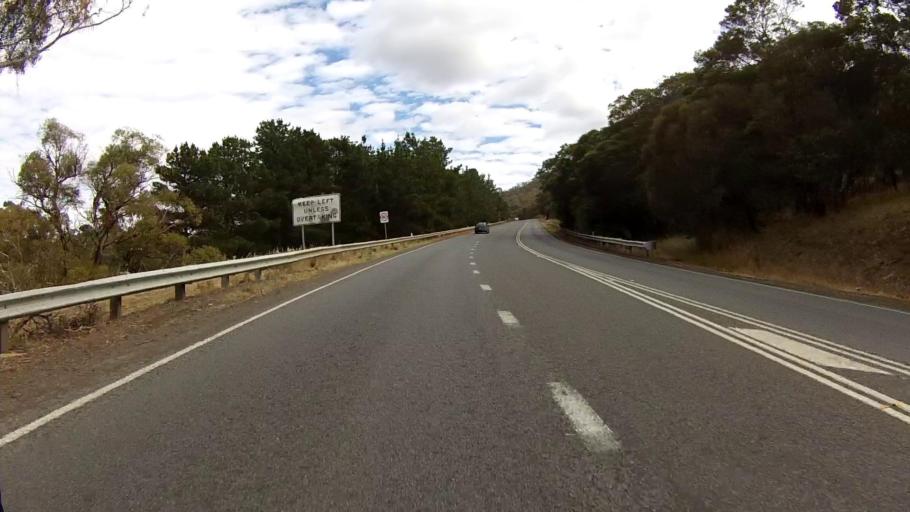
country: AU
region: Tasmania
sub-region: Glenorchy
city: Goodwood
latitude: -42.8101
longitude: 147.3021
